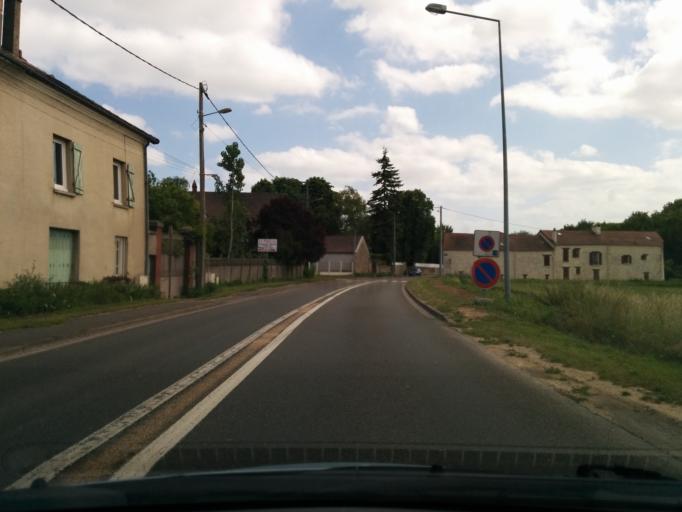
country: FR
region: Ile-de-France
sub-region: Departement des Yvelines
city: Epone
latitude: 48.9508
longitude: 1.8333
